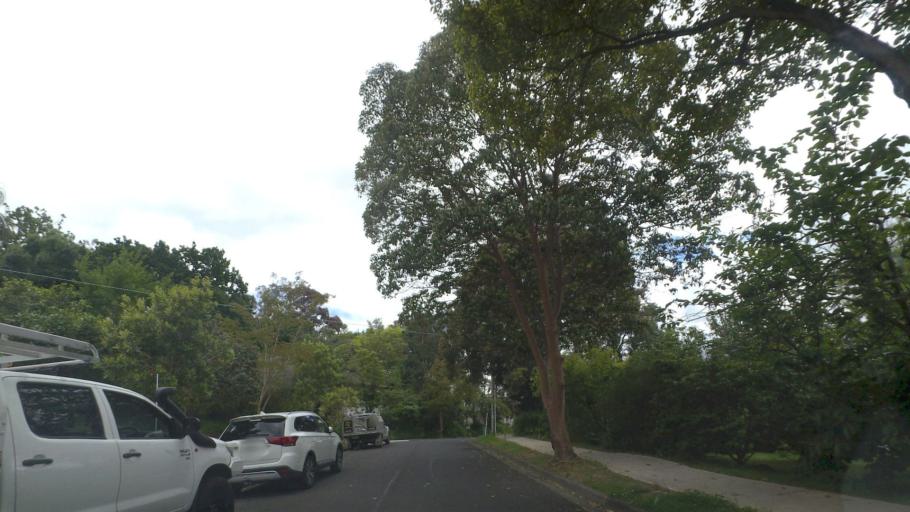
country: AU
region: Victoria
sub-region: Maroondah
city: Croydon North
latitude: -37.7860
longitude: 145.2815
